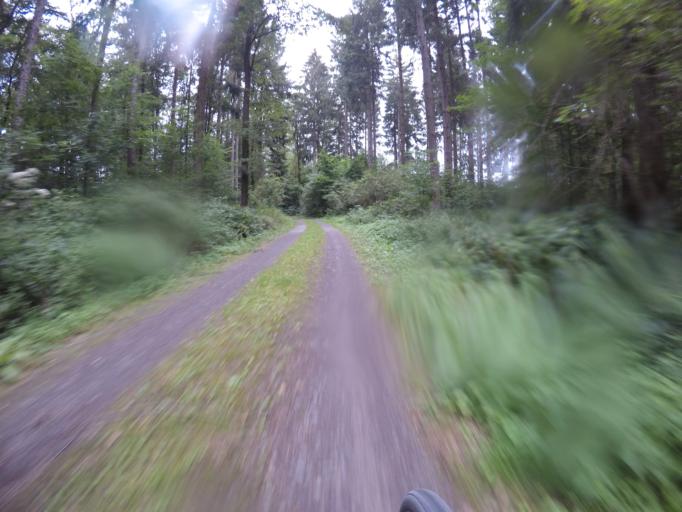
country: DE
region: Baden-Wuerttemberg
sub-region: Regierungsbezirk Stuttgart
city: Schonaich
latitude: 48.6906
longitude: 9.0514
